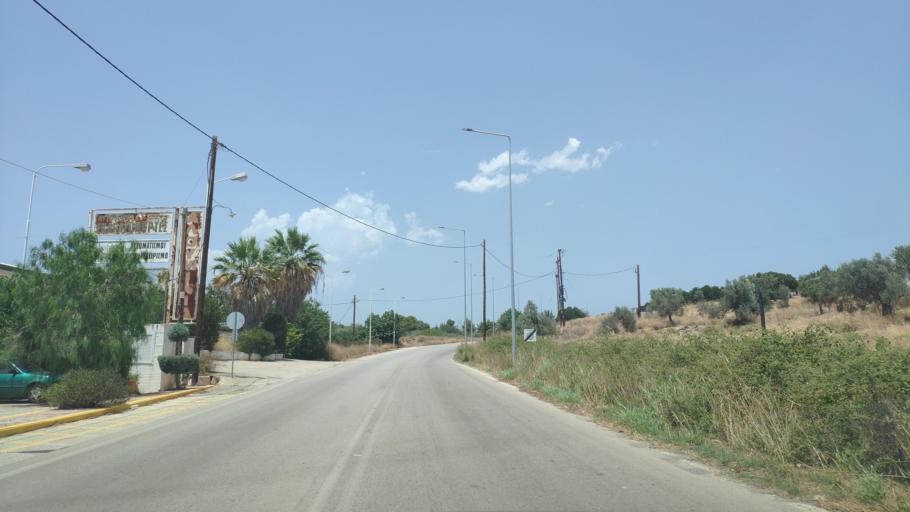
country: GR
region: Peloponnese
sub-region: Nomos Argolidos
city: Kranidi
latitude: 37.3661
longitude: 23.1621
